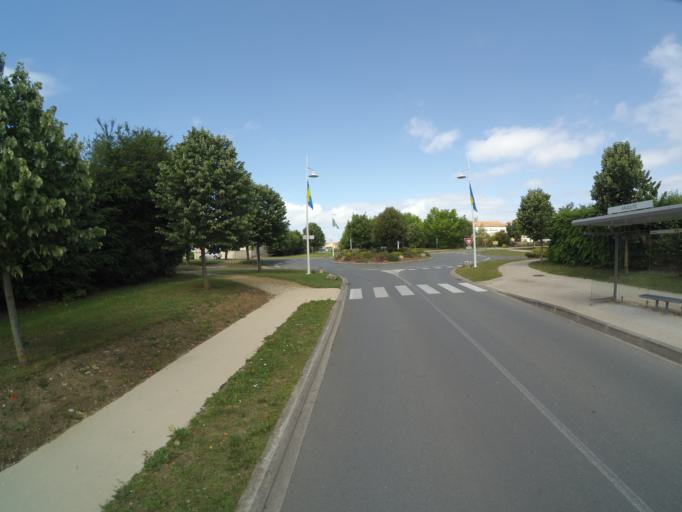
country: FR
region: Poitou-Charentes
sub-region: Departement de la Charente-Maritime
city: Chatelaillon-Plage
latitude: 46.0580
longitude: -1.0826
